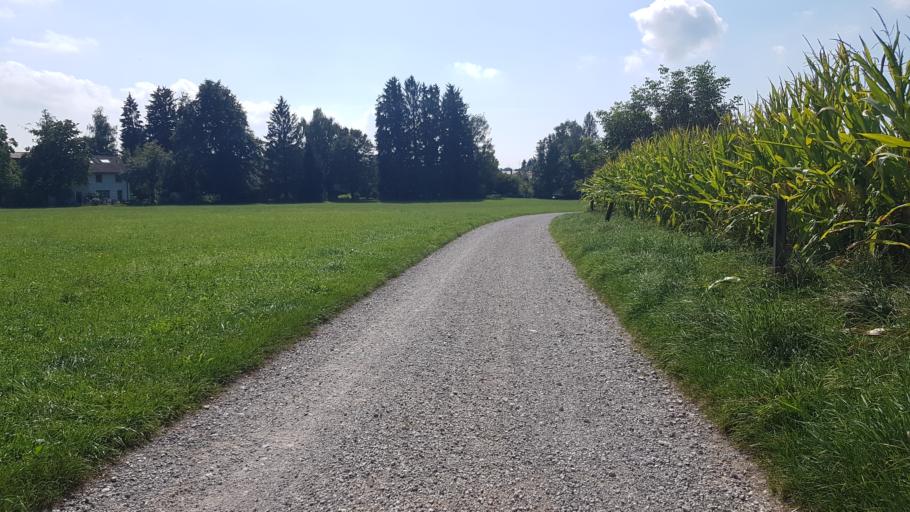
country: DE
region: Bavaria
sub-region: Upper Bavaria
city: Worthsee
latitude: 48.0435
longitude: 11.1935
